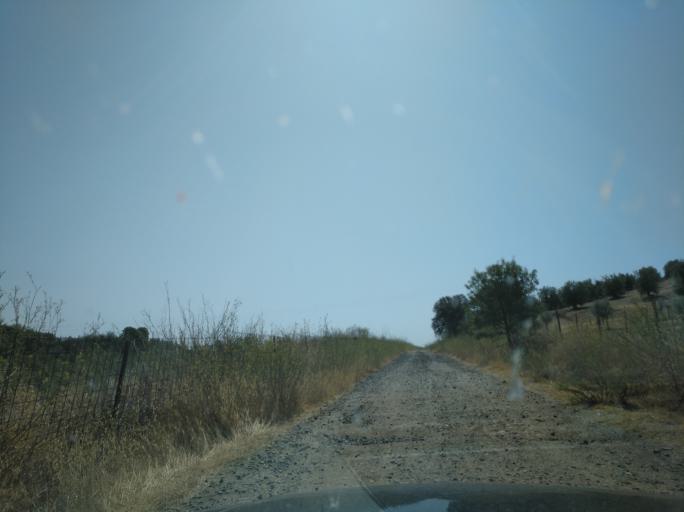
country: PT
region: Portalegre
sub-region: Campo Maior
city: Campo Maior
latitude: 39.0613
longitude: -7.0097
